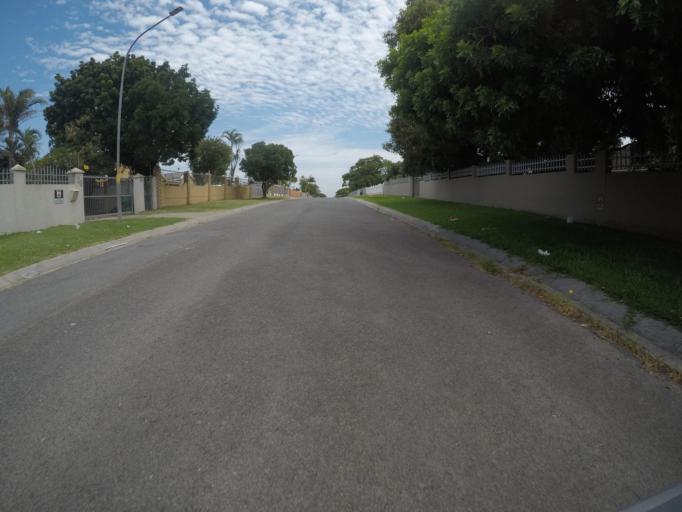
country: ZA
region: Eastern Cape
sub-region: Buffalo City Metropolitan Municipality
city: East London
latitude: -32.9828
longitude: 27.8644
